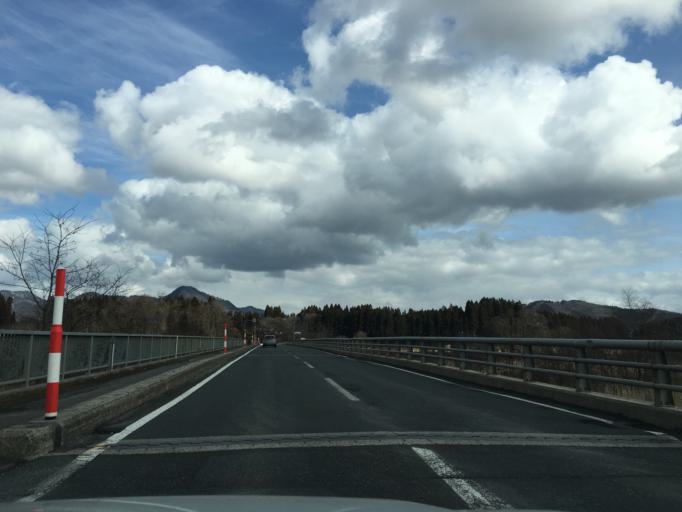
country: JP
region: Akita
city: Odate
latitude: 40.2110
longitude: 140.5798
